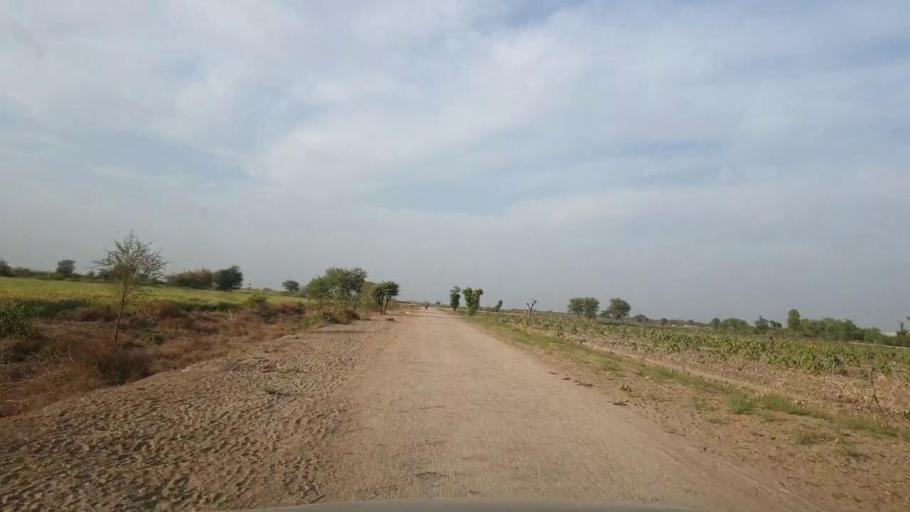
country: PK
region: Sindh
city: Kunri
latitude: 25.2252
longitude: 69.5031
